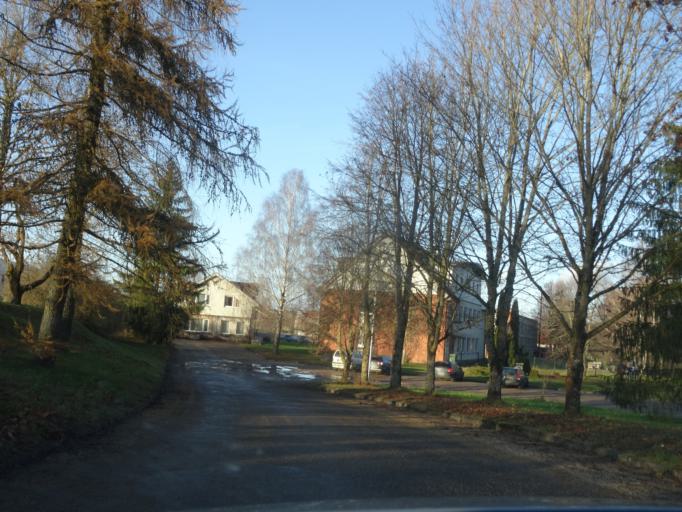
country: LV
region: Kuldigas Rajons
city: Kuldiga
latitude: 56.9768
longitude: 21.9690
